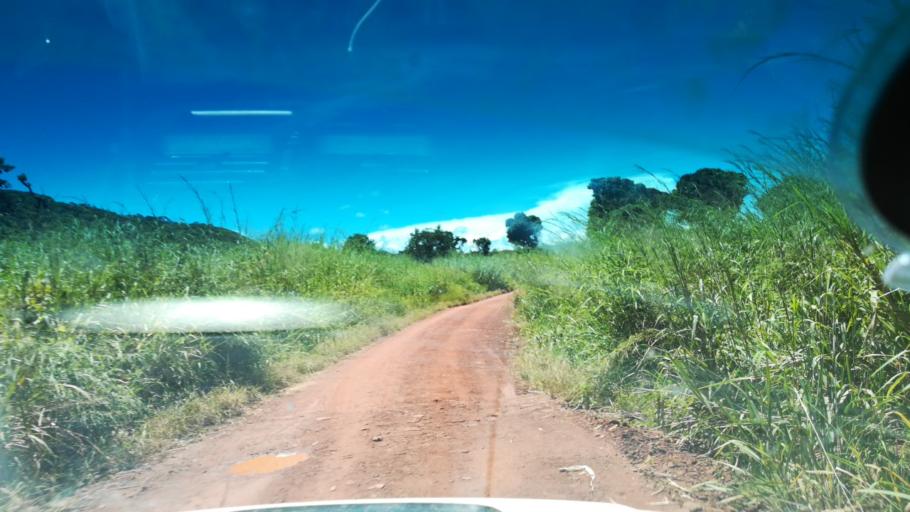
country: ZM
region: Luapula
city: Nchelenge
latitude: -8.7549
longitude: 28.6571
